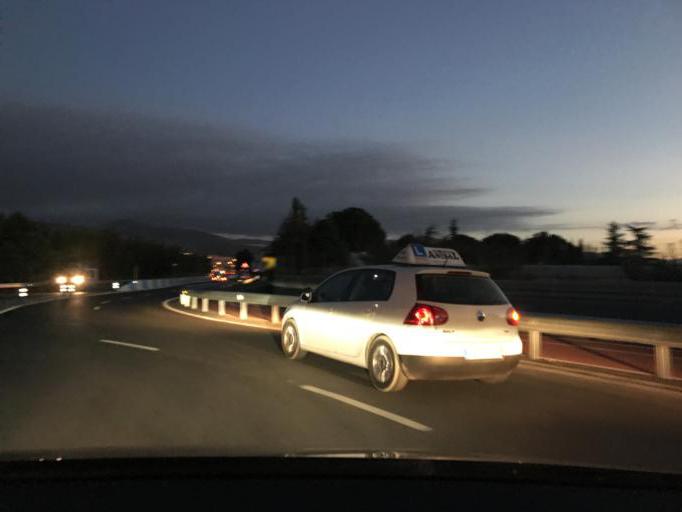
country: ES
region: Andalusia
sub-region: Provincia de Granada
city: Cajar
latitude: 37.1419
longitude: -3.5908
